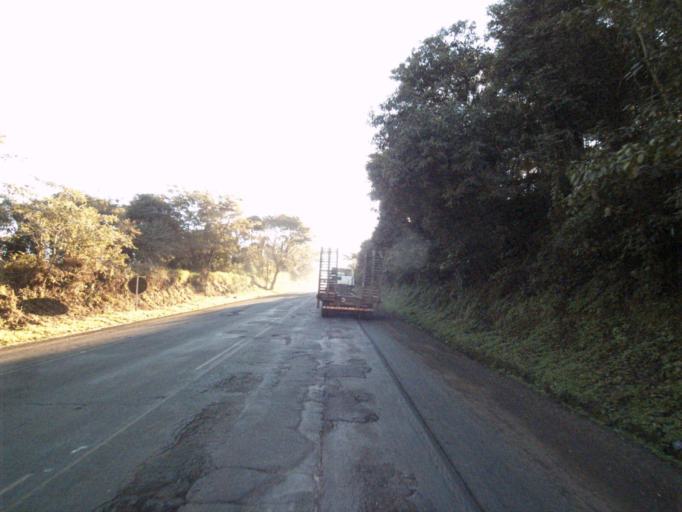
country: BR
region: Santa Catarina
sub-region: Chapeco
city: Chapeco
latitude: -26.8937
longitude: -52.9256
